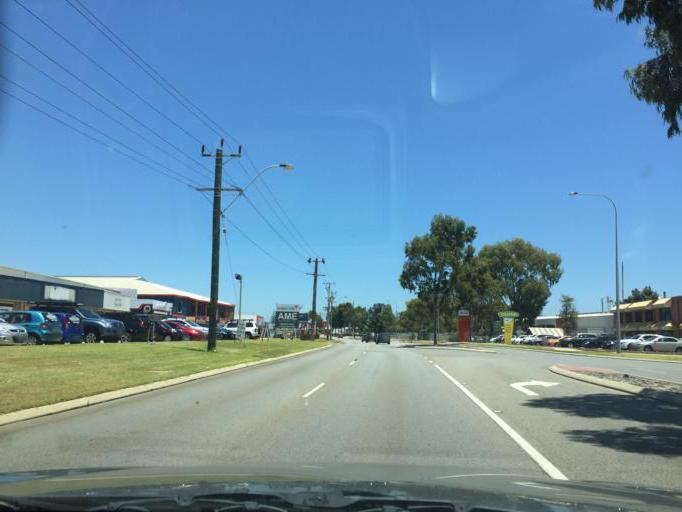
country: AU
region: Western Australia
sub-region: Canning
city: Canning Vale
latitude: -32.0584
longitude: 115.9117
